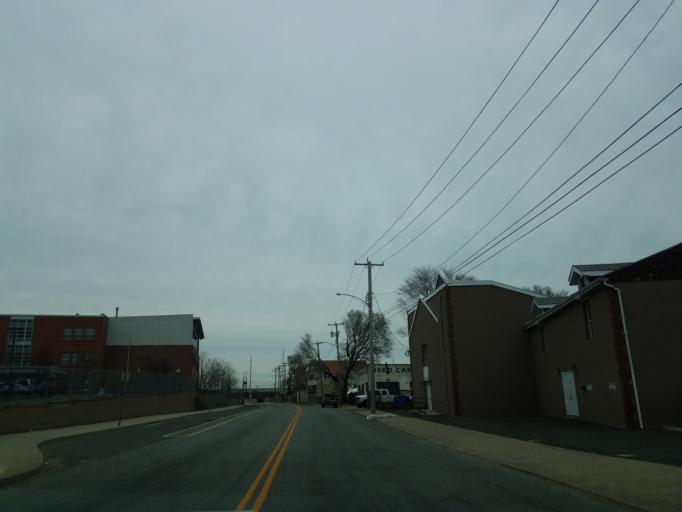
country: US
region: Connecticut
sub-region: Fairfield County
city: Bridgeport
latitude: 41.1821
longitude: -73.1742
